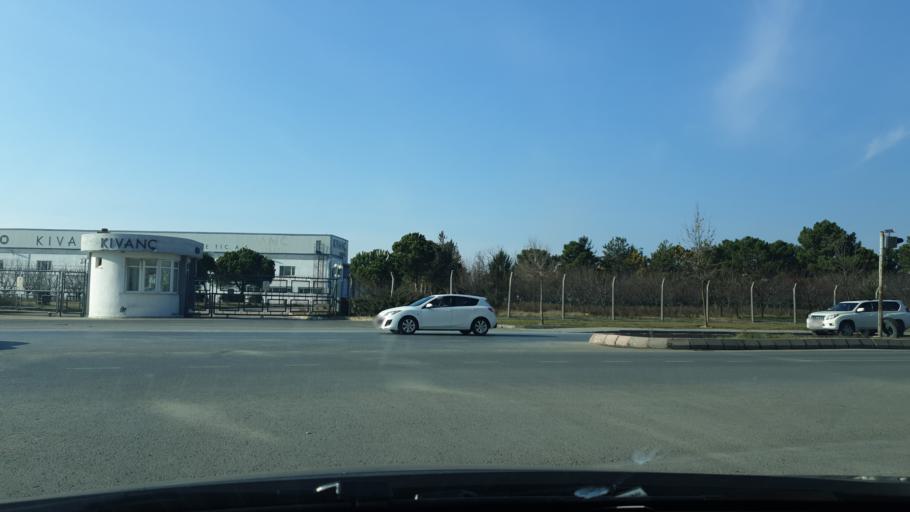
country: TR
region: Tekirdag
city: Cerkezkoey
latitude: 41.2944
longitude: 27.9954
